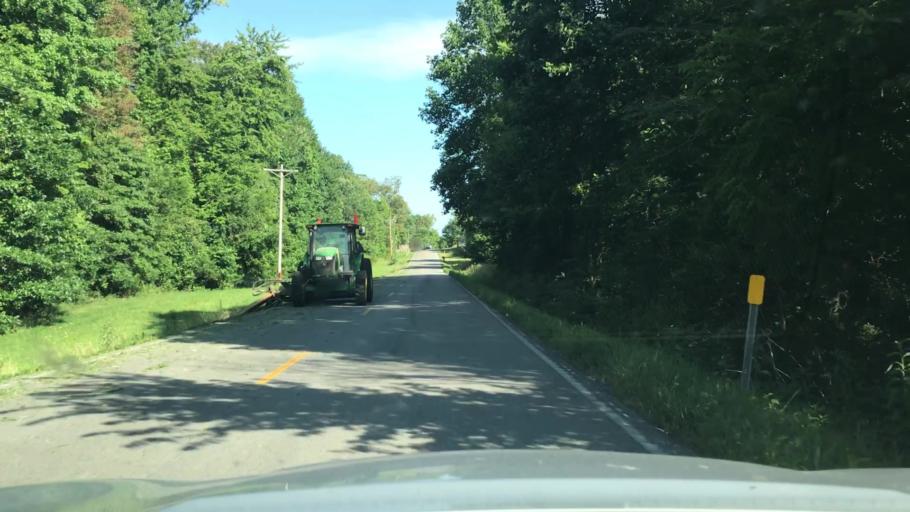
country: US
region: Kentucky
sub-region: Muhlenberg County
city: Greenville
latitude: 37.1300
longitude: -87.1386
